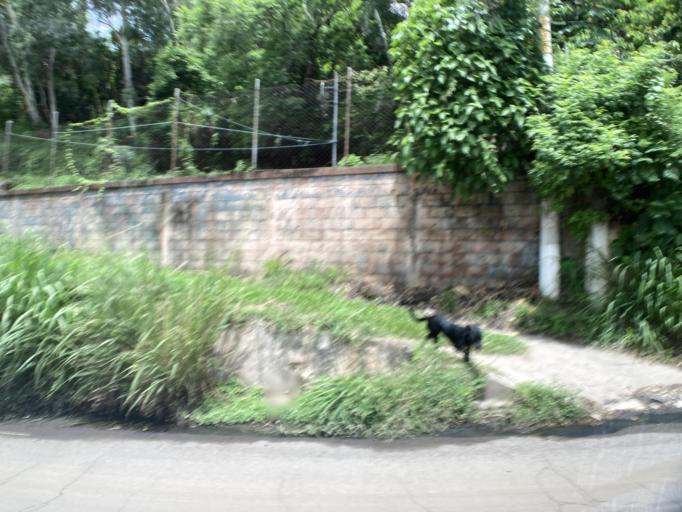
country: GT
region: Guatemala
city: Villa Canales
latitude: 14.4493
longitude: -90.5660
